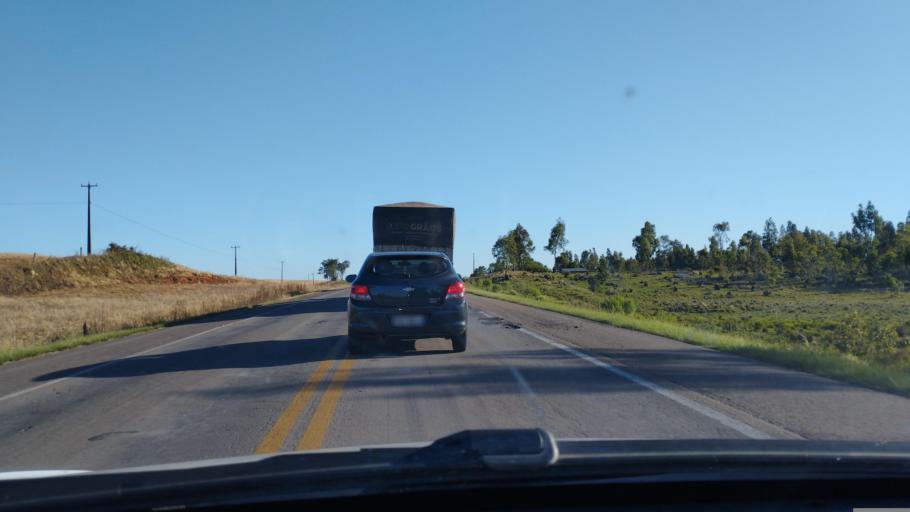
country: BR
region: Rio Grande do Sul
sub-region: Julio De Castilhos
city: Julio de Castilhos
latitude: -29.3779
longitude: -53.6706
